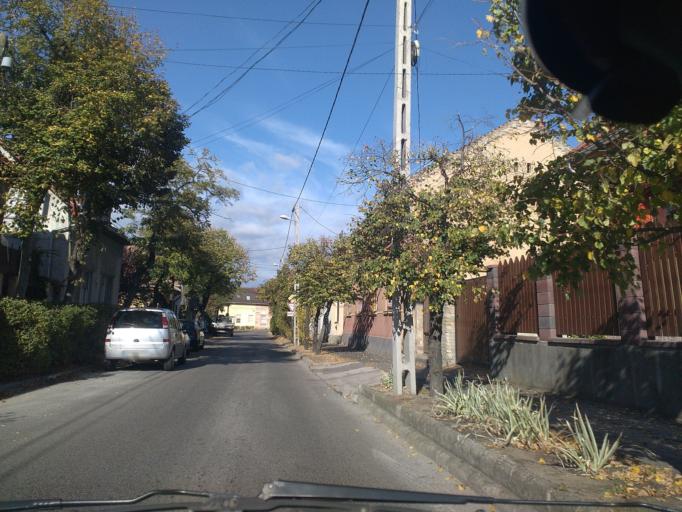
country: HU
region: Budapest
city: Budapest XX. keruelet
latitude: 47.4364
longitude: 19.1139
